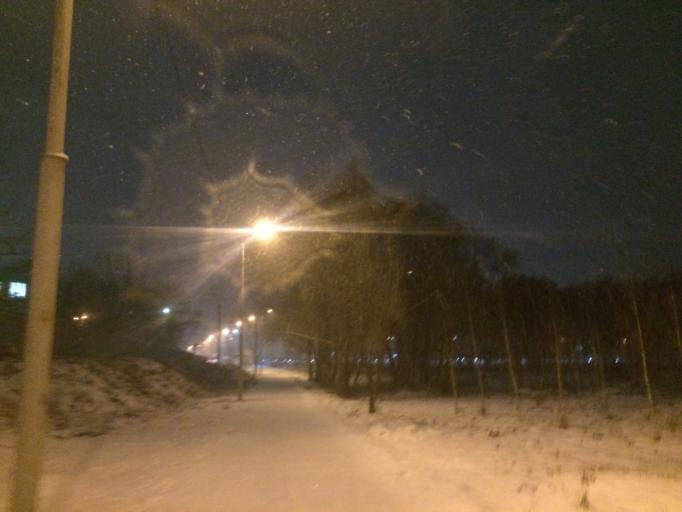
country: RU
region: Tula
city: Tula
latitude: 54.1755
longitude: 37.5900
